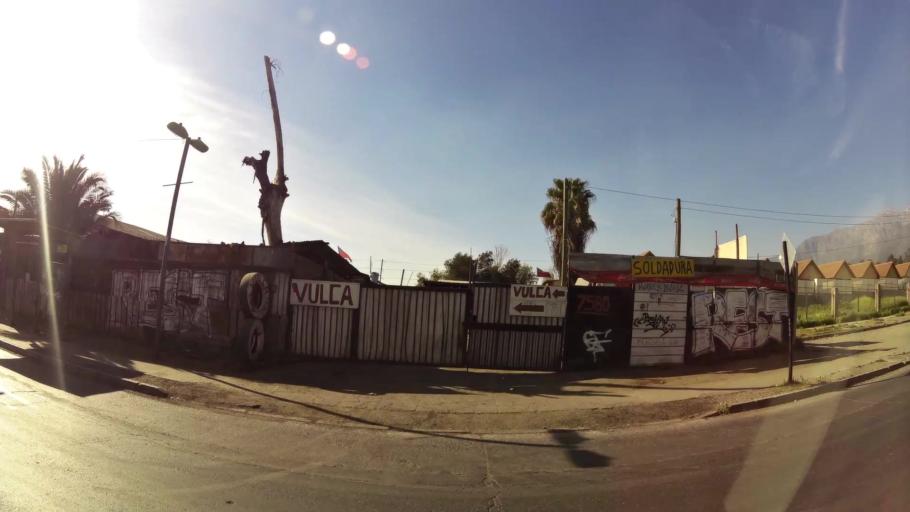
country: CL
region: Santiago Metropolitan
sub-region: Provincia de Santiago
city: Villa Presidente Frei, Nunoa, Santiago, Chile
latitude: -33.5121
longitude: -70.5532
